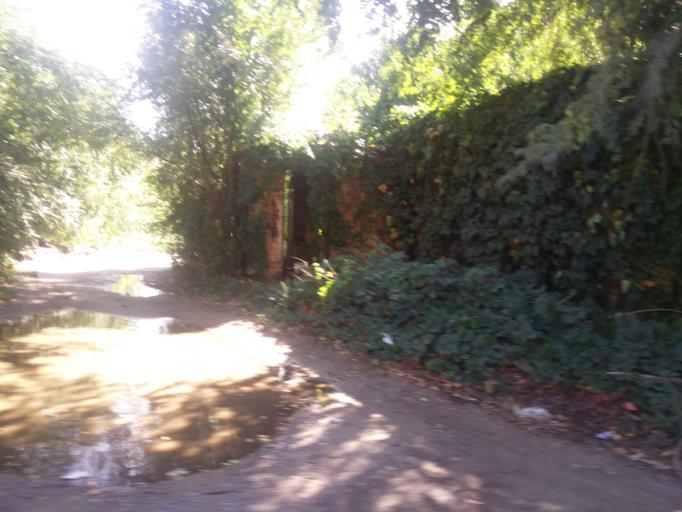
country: RU
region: Voronezj
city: Voronezh
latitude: 51.6472
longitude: 39.1609
